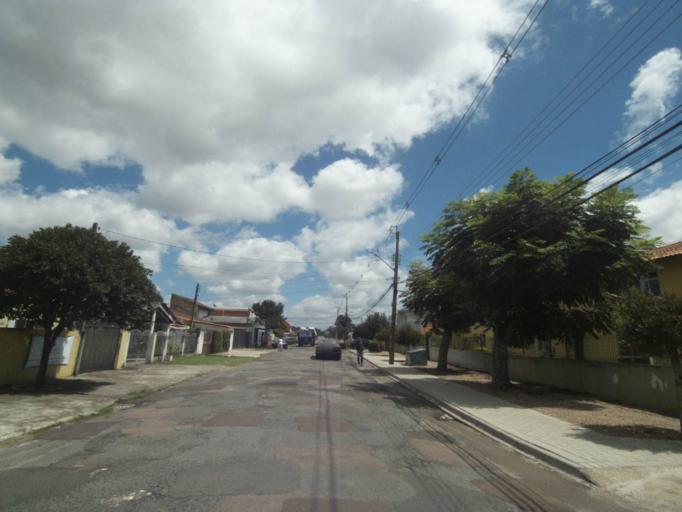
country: BR
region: Parana
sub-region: Pinhais
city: Pinhais
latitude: -25.4408
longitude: -49.2061
